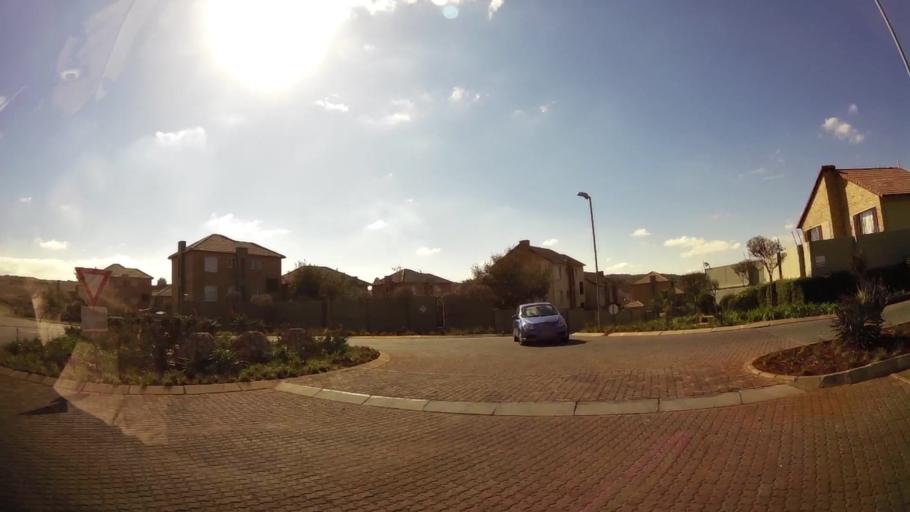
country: ZA
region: Gauteng
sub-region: West Rand District Municipality
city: Krugersdorp
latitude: -26.0863
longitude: 27.8152
